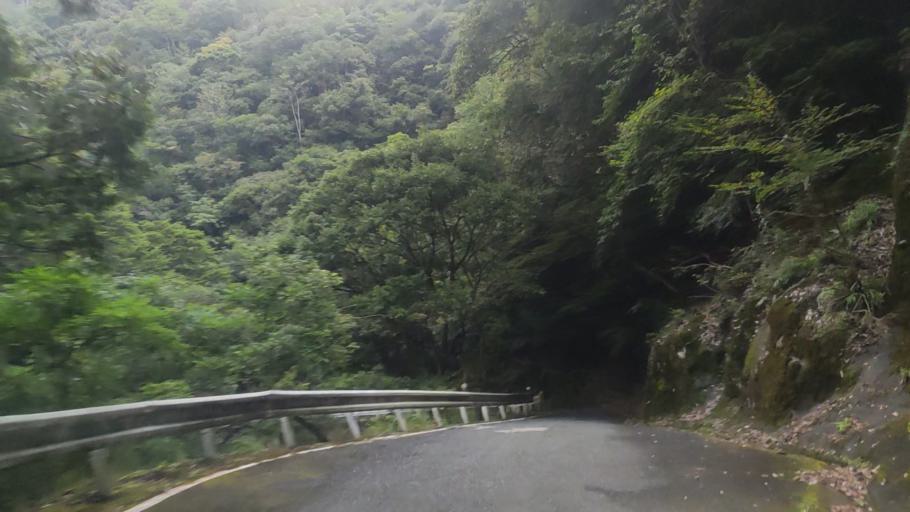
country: JP
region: Wakayama
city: Koya
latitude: 34.2497
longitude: 135.6536
